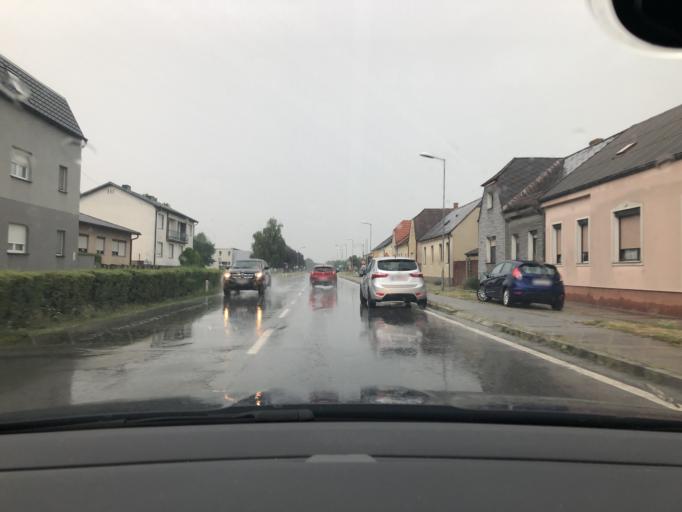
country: AT
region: Lower Austria
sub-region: Politischer Bezirk Ganserndorf
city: Marchegg
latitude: 48.2640
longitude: 16.9093
